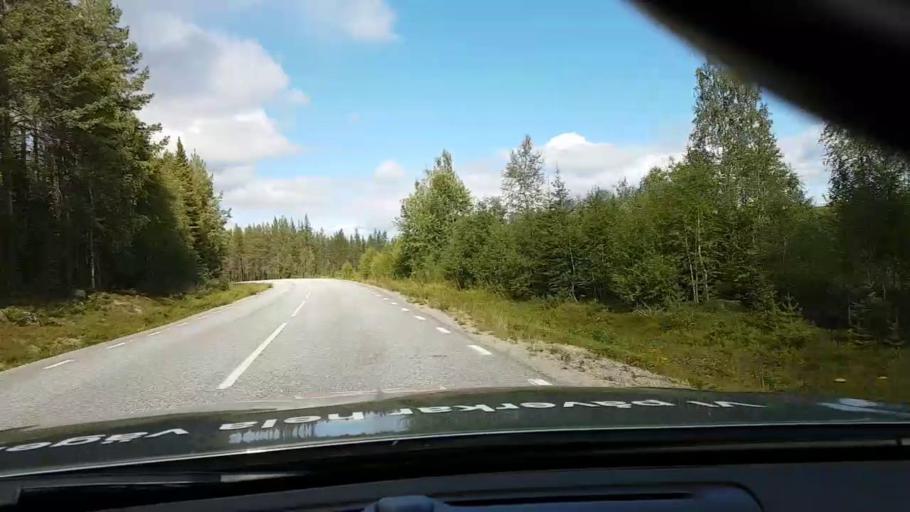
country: SE
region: Vaesternorrland
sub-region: OErnskoeldsviks Kommun
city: Bredbyn
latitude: 63.6882
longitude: 17.7705
